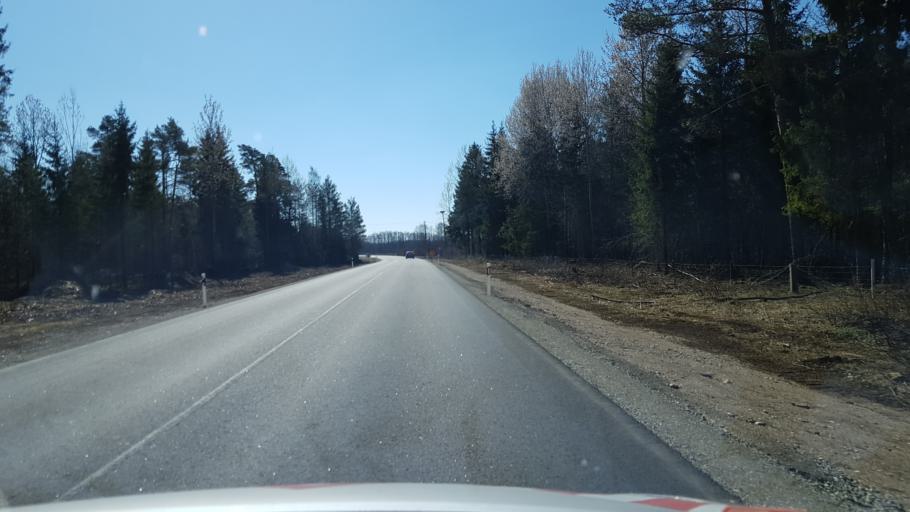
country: EE
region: Laeaene-Virumaa
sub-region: Vinni vald
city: Vinni
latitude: 59.0662
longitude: 26.6382
